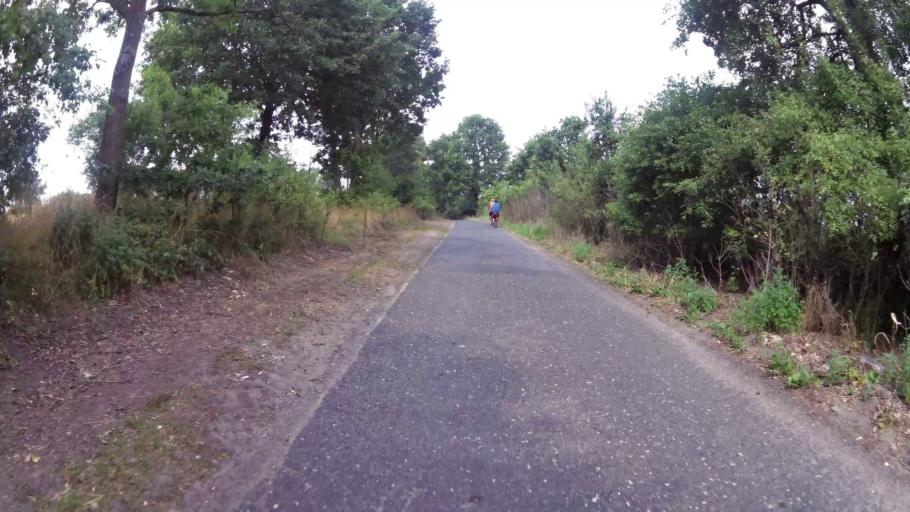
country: PL
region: West Pomeranian Voivodeship
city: Trzcinsko Zdroj
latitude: 52.9042
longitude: 14.6660
